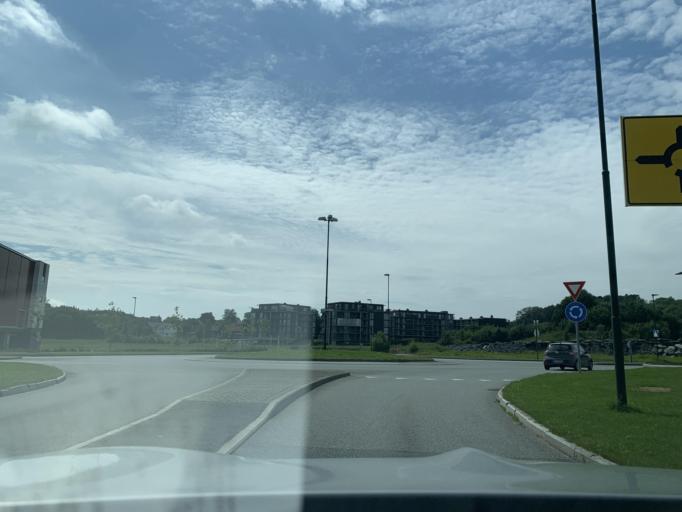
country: NO
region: Rogaland
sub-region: Sola
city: Sola
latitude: 58.8951
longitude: 5.6796
